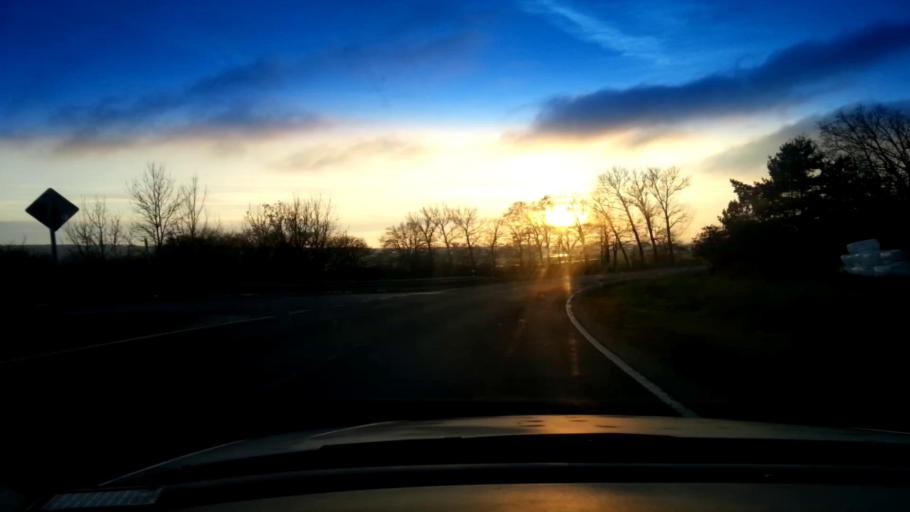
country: DE
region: Bavaria
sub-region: Upper Franconia
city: Frensdorf
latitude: 49.7907
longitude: 10.8788
